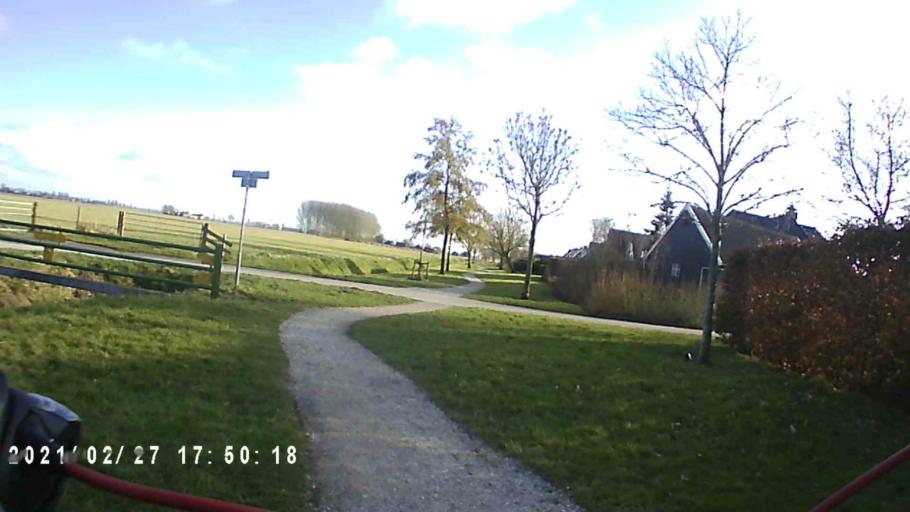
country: NL
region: Groningen
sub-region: Gemeente Bedum
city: Bedum
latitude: 53.3066
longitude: 6.6122
